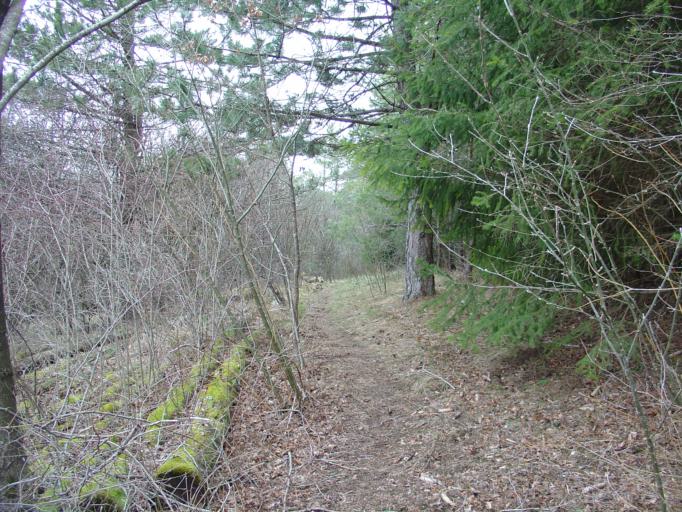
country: FR
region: Lorraine
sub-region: Departement de Meurthe-et-Moselle
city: Blenod-les-Toul
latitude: 48.5415
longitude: 5.8195
